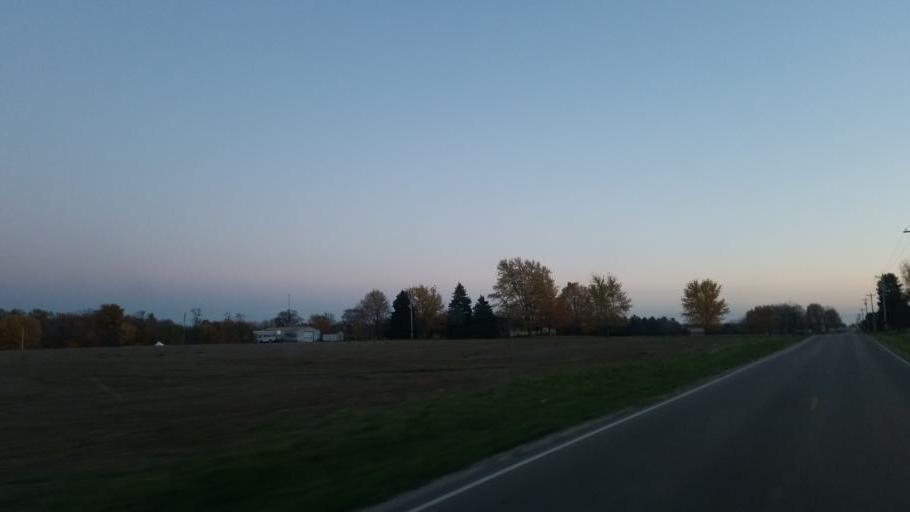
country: US
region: Ohio
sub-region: Huron County
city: Plymouth
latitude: 40.9538
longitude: -82.7433
